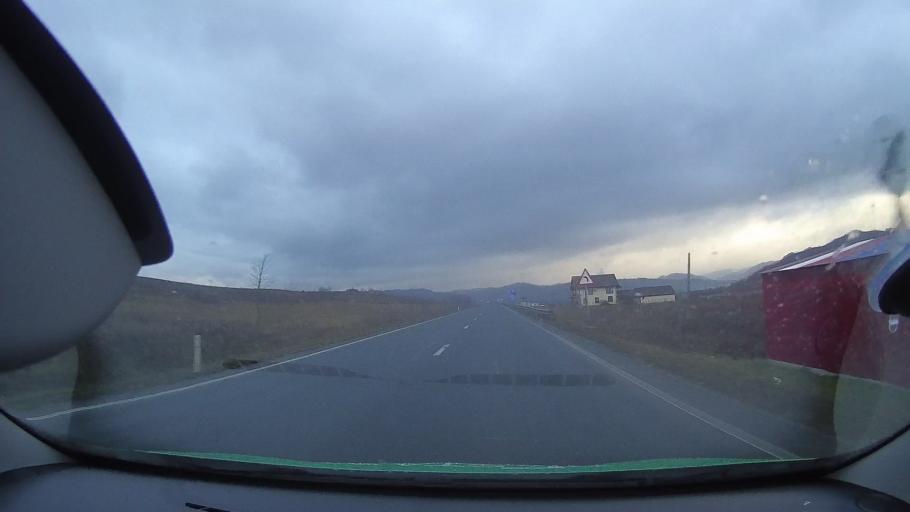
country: RO
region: Hunedoara
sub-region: Comuna Ribita
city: Ribita
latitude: 46.1584
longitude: 22.7630
